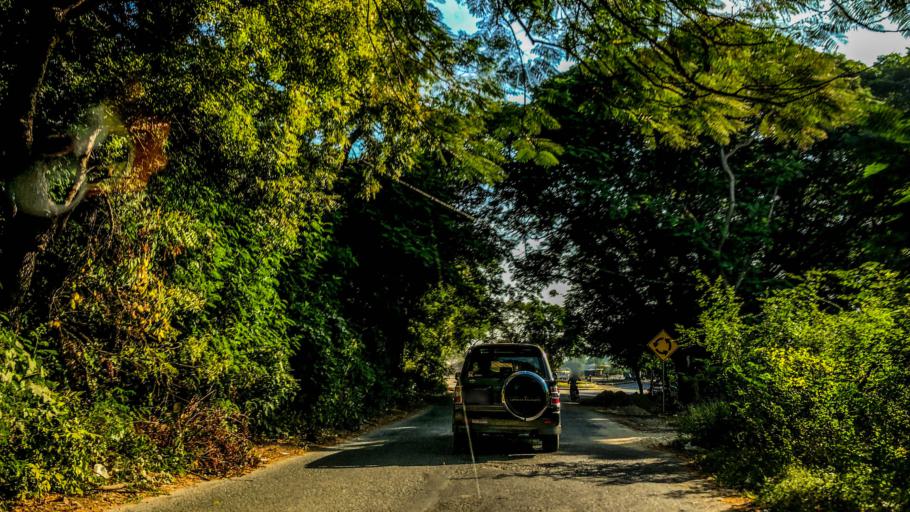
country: MM
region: Sagain
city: Sagaing
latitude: 21.8669
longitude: 95.9988
